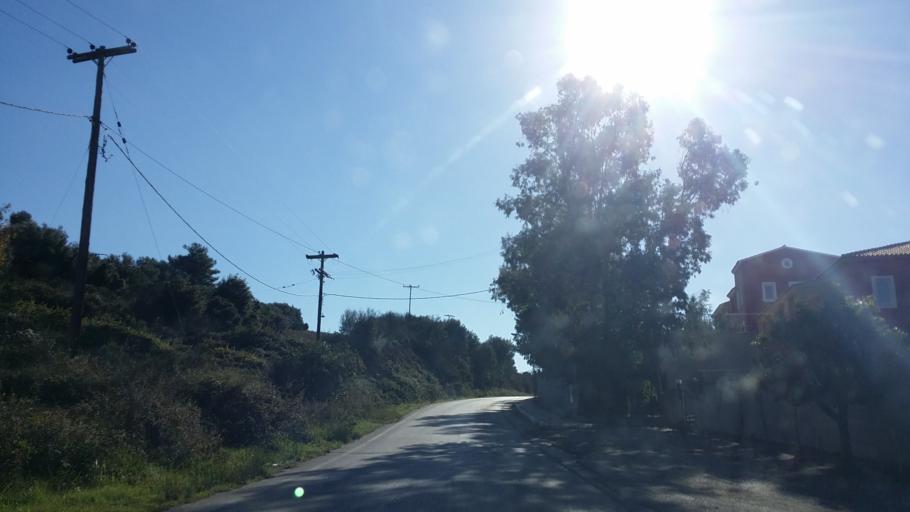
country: GR
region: West Greece
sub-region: Nomos Aitolias kai Akarnanias
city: Palairos
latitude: 38.7728
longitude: 20.8811
